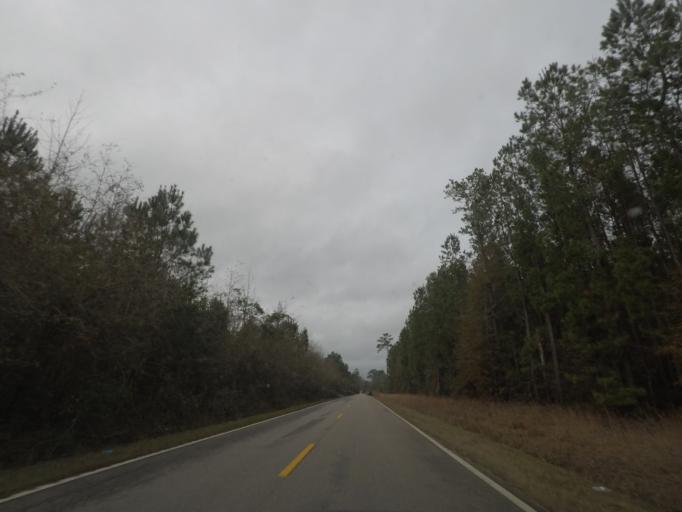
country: US
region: South Carolina
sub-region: Colleton County
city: Walterboro
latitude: 32.8749
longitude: -80.4916
